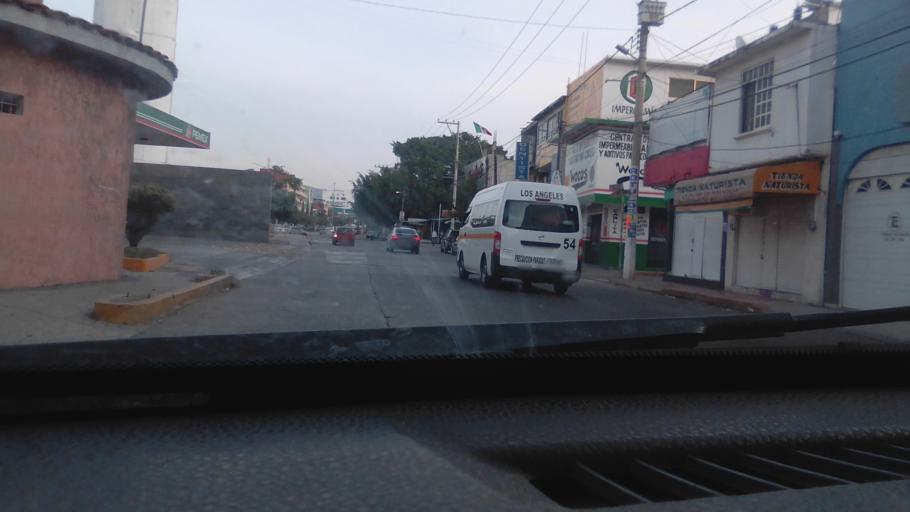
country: MX
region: Guerrero
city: Chilpancingo de los Bravos
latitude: 17.5593
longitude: -99.5058
